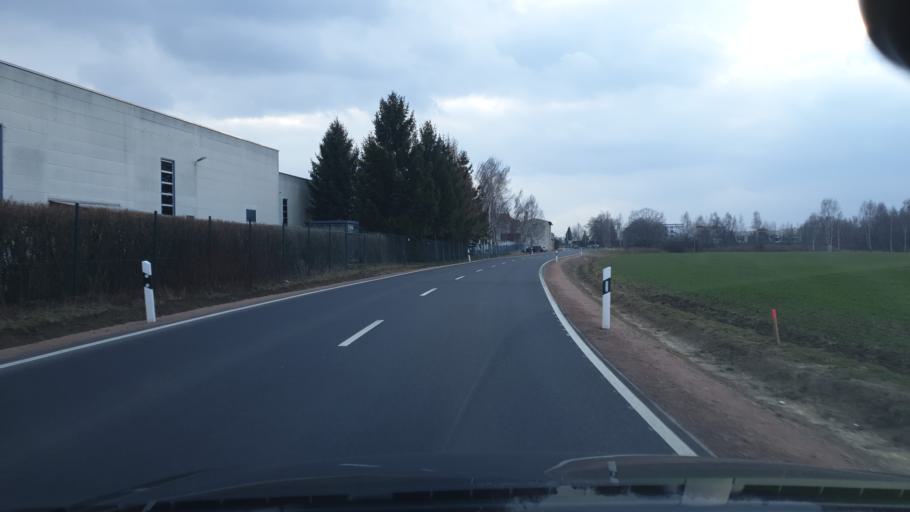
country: DE
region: Saxony
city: Altmittweida
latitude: 50.9891
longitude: 12.9493
